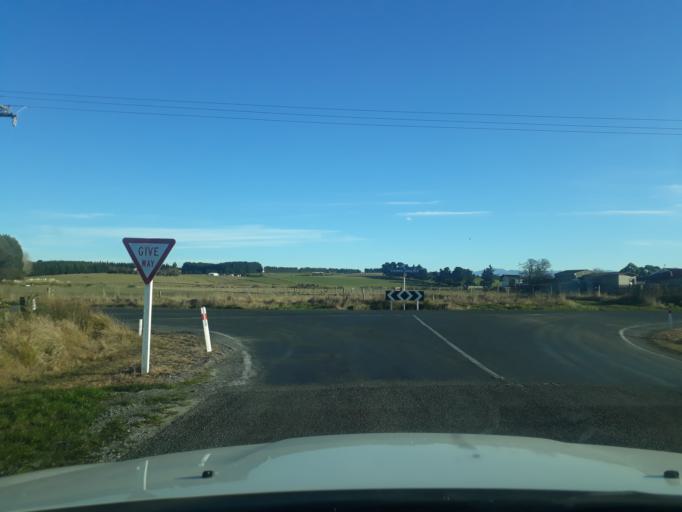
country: NZ
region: Canterbury
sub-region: Timaru District
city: Timaru
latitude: -44.3421
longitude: 171.2003
